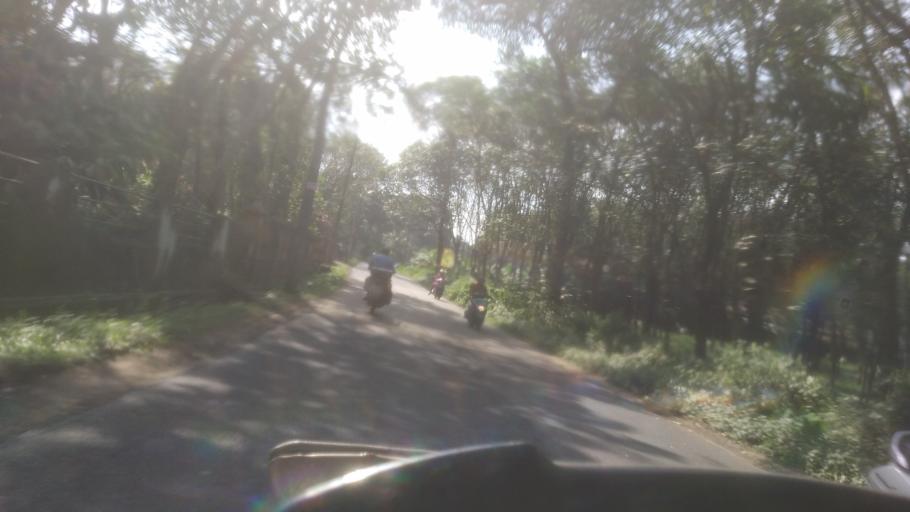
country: IN
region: Kerala
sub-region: Ernakulam
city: Kotamangalam
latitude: 10.0022
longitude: 76.7313
